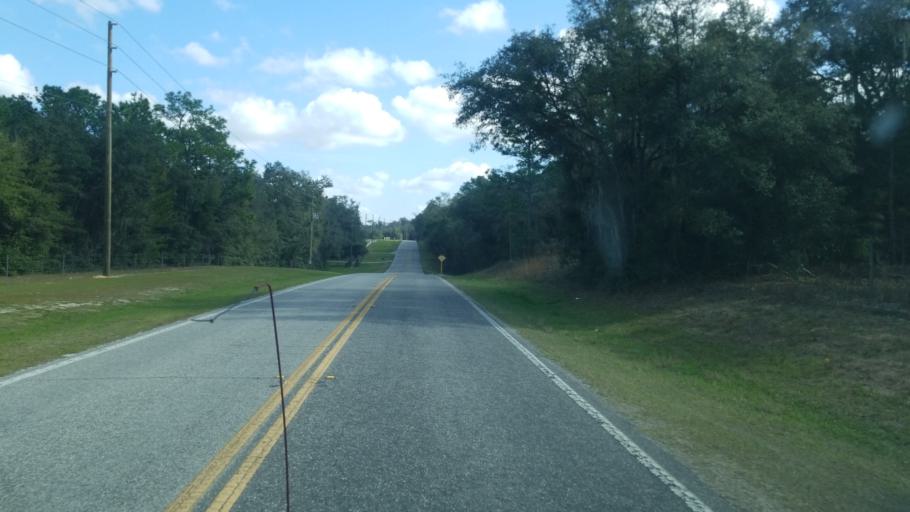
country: US
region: Florida
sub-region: Citrus County
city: Floral City
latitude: 28.7280
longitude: -82.3170
